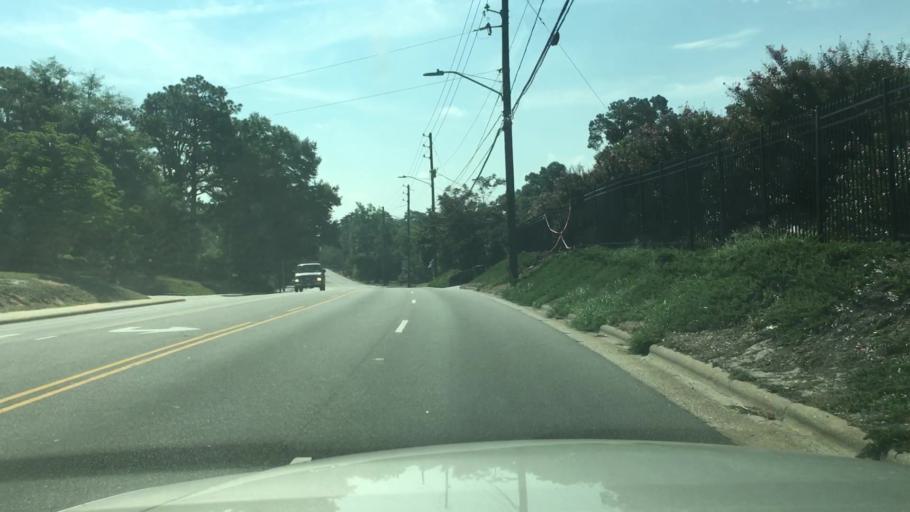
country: US
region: North Carolina
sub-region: Cumberland County
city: Fayetteville
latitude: 35.0607
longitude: -78.9159
